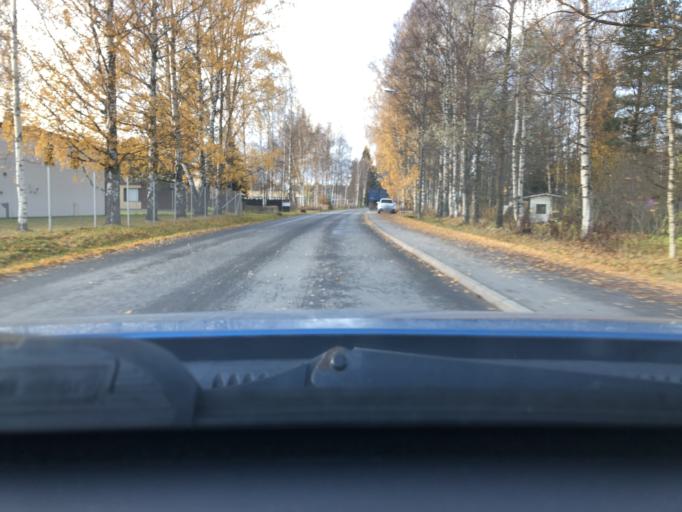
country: FI
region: Pirkanmaa
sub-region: Tampere
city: Kangasala
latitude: 61.4659
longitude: 24.0324
